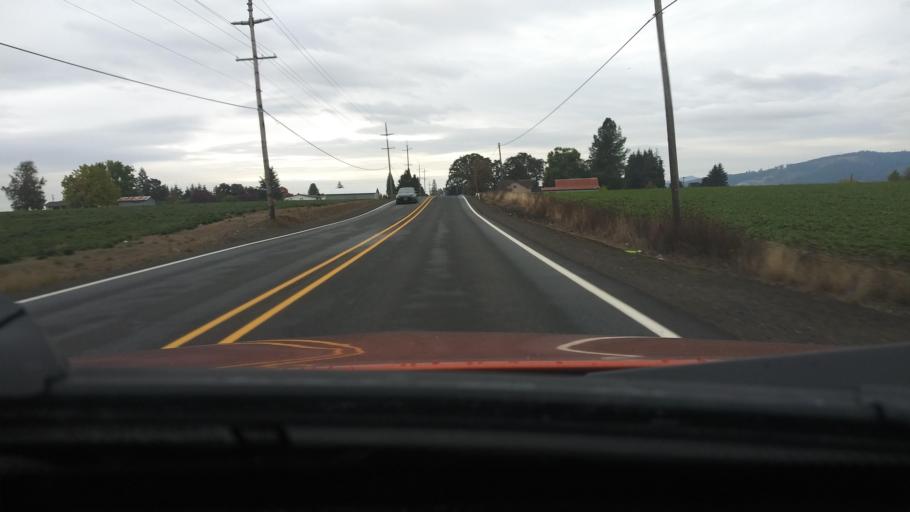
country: US
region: Oregon
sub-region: Washington County
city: Banks
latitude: 45.5959
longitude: -123.1145
